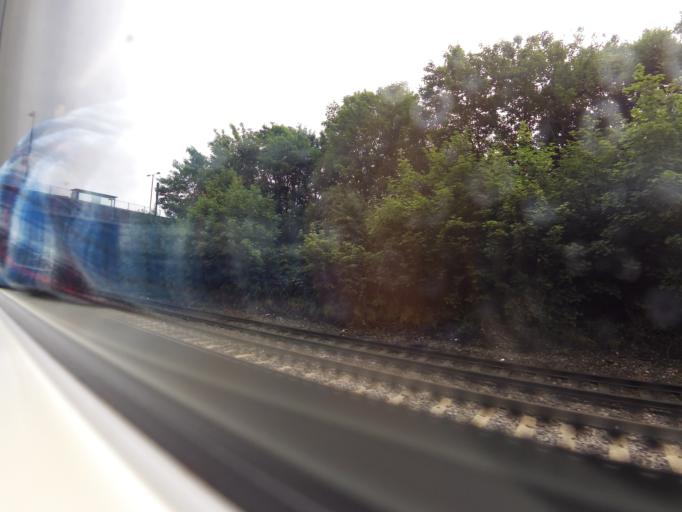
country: GB
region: England
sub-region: Greater London
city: Catford
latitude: 51.4494
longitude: -0.0461
